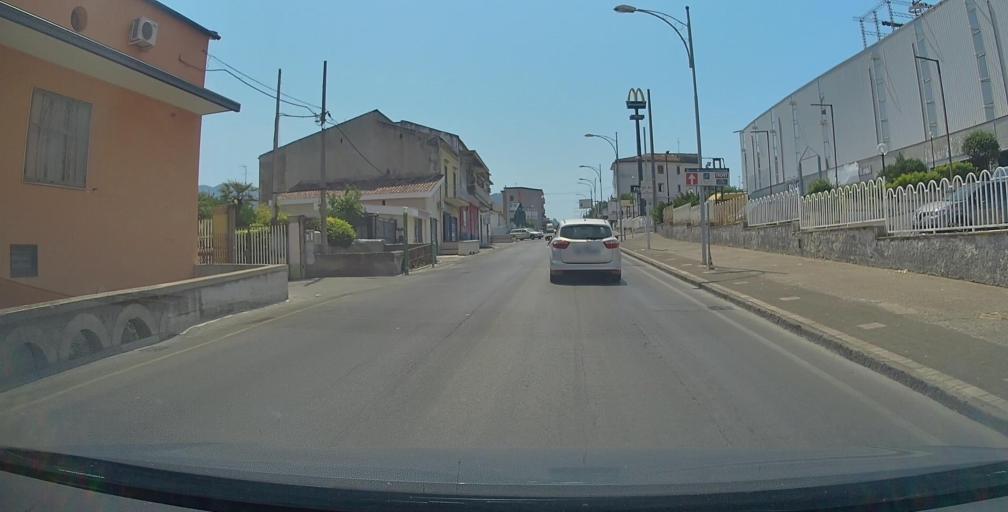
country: IT
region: Campania
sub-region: Provincia di Salerno
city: Nocera Superiore
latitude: 40.7289
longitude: 14.6898
